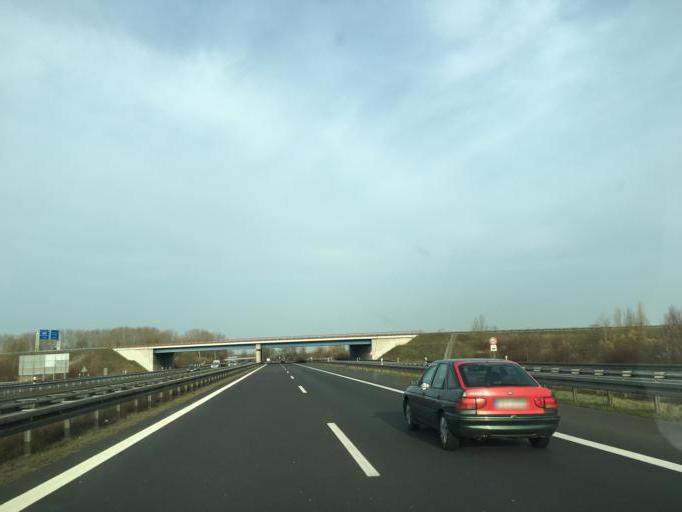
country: DE
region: Brandenburg
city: Leegebruch
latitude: 52.7041
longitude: 13.2047
